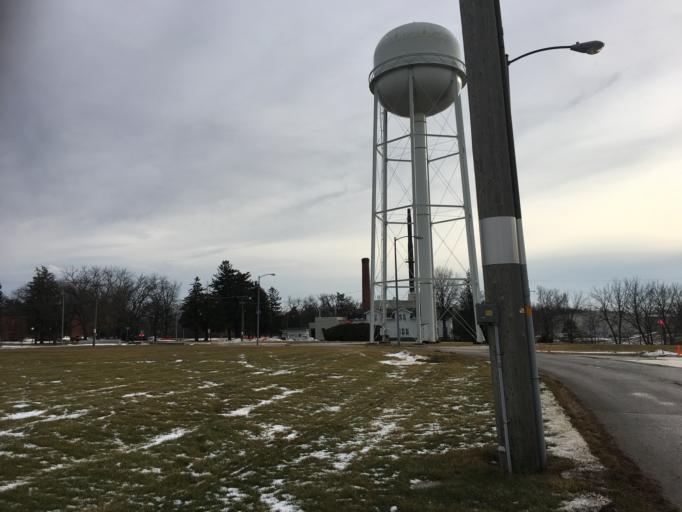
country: US
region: Iowa
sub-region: Johnson County
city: Coralville
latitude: 41.7072
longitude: -91.6040
